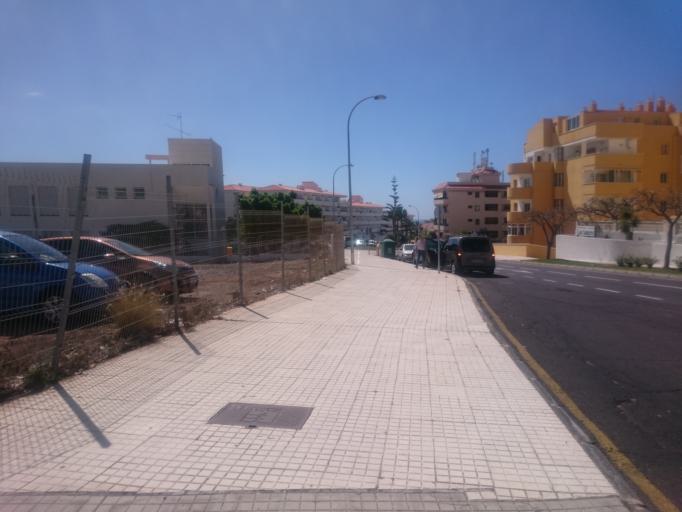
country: ES
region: Canary Islands
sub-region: Provincia de Santa Cruz de Tenerife
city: Playa de las Americas
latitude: 28.0554
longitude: -16.7079
